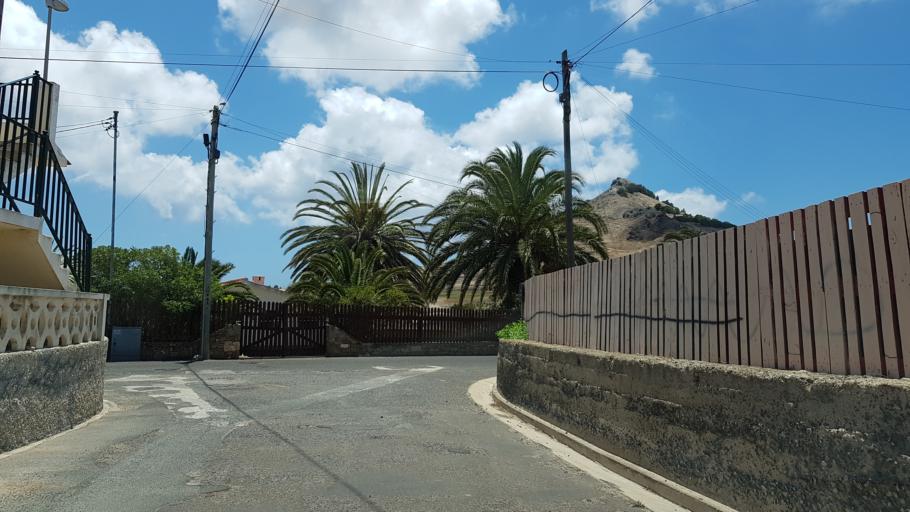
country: PT
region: Madeira
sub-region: Porto Santo
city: Vila de Porto Santo
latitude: 33.0545
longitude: -16.3655
